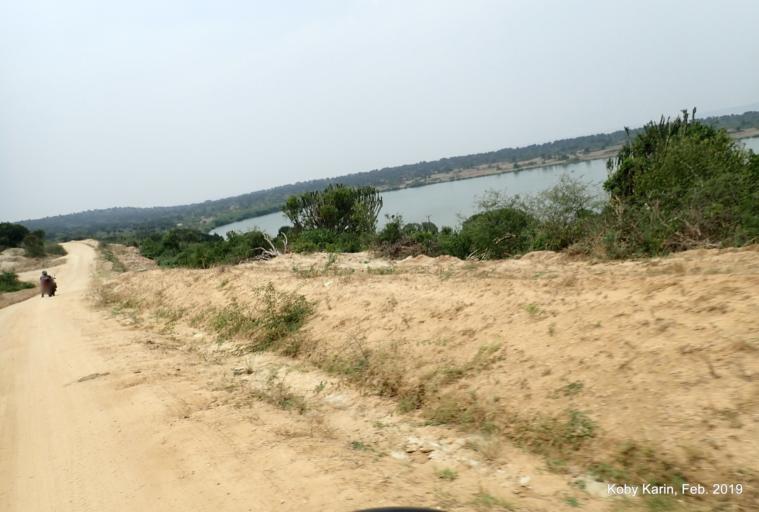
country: UG
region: Western Region
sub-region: Rubirizi District
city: Rubirizi
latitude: -0.1823
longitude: 29.9019
